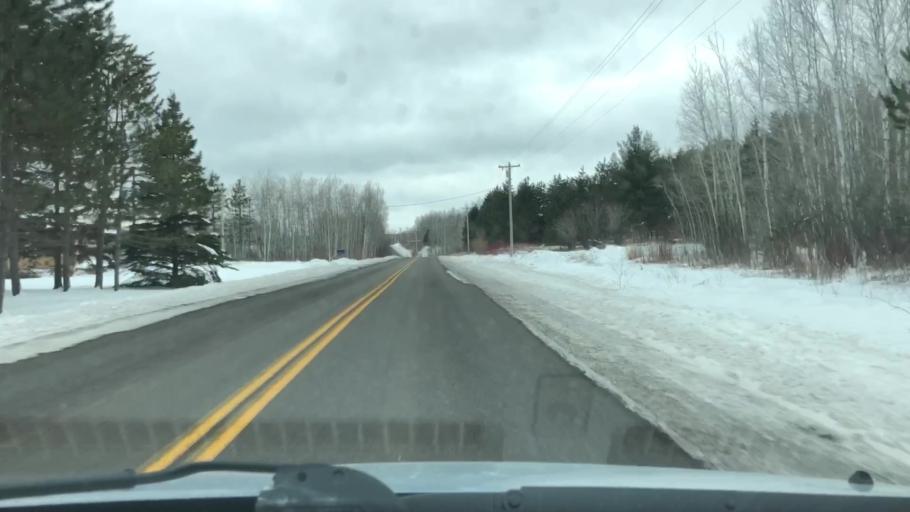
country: US
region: Minnesota
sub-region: Saint Louis County
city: Proctor
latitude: 46.7001
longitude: -92.2820
